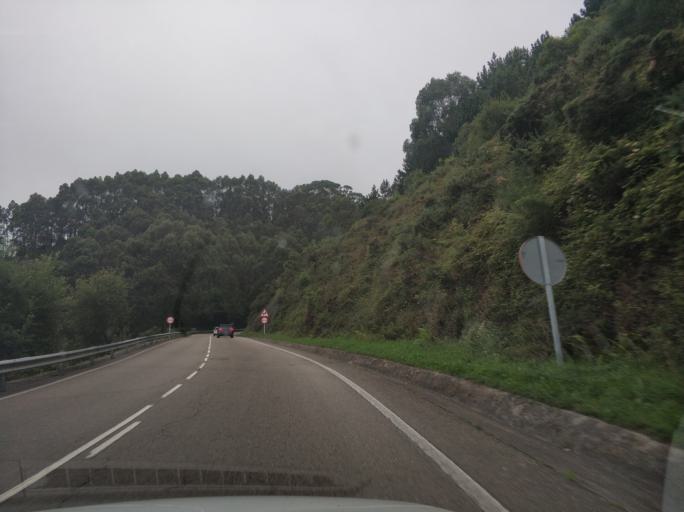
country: ES
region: Asturias
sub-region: Province of Asturias
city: Cudillero
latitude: 43.5667
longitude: -6.1534
